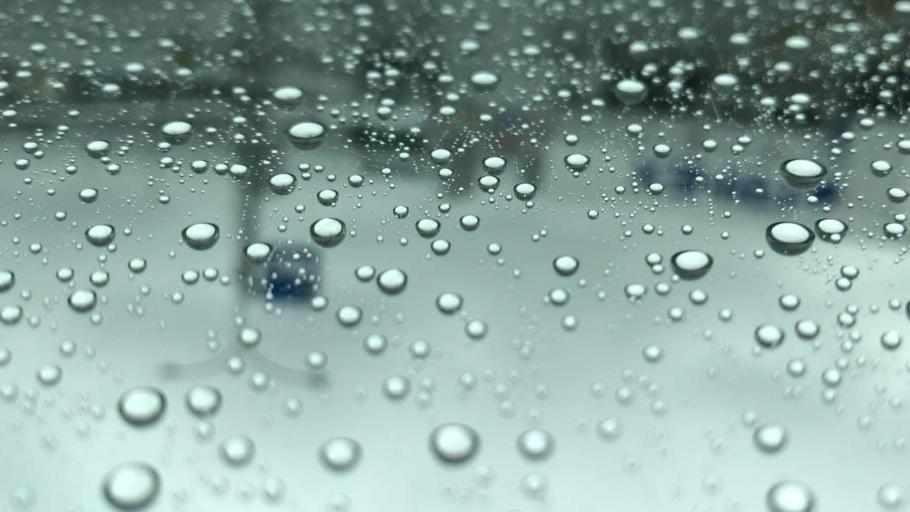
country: JP
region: Hokkaido
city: Otaru
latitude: 43.1891
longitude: 141.0147
